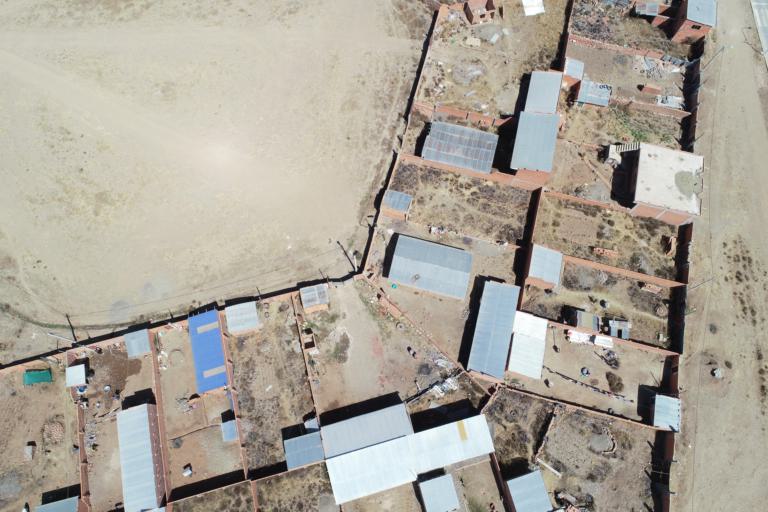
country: BO
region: La Paz
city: La Paz
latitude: -16.5919
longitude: -68.2130
